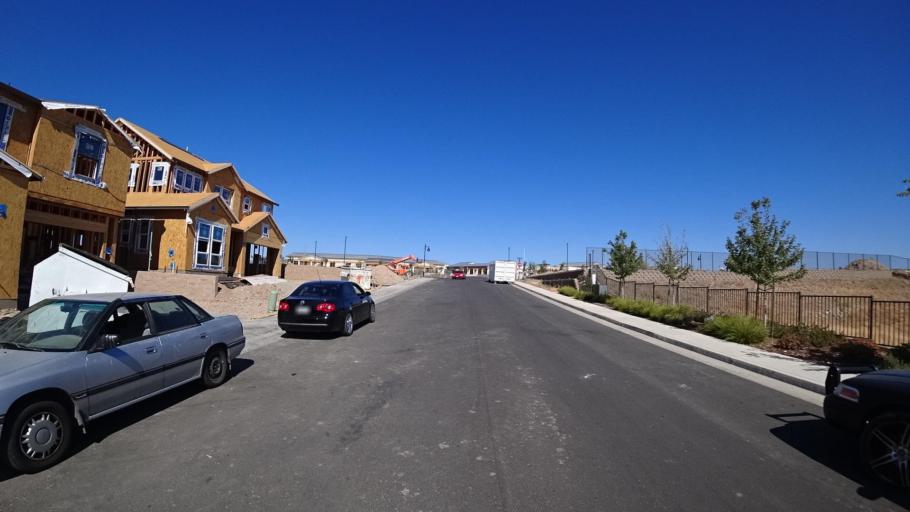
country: US
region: California
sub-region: Placer County
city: Rocklin
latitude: 38.8308
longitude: -121.2620
